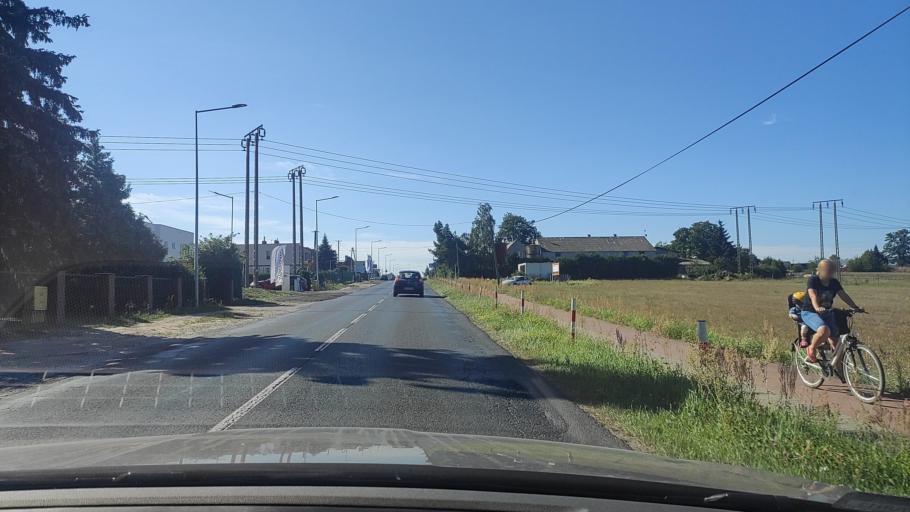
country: PL
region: Greater Poland Voivodeship
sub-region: Powiat poznanski
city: Kobylnica
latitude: 52.4374
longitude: 17.0742
